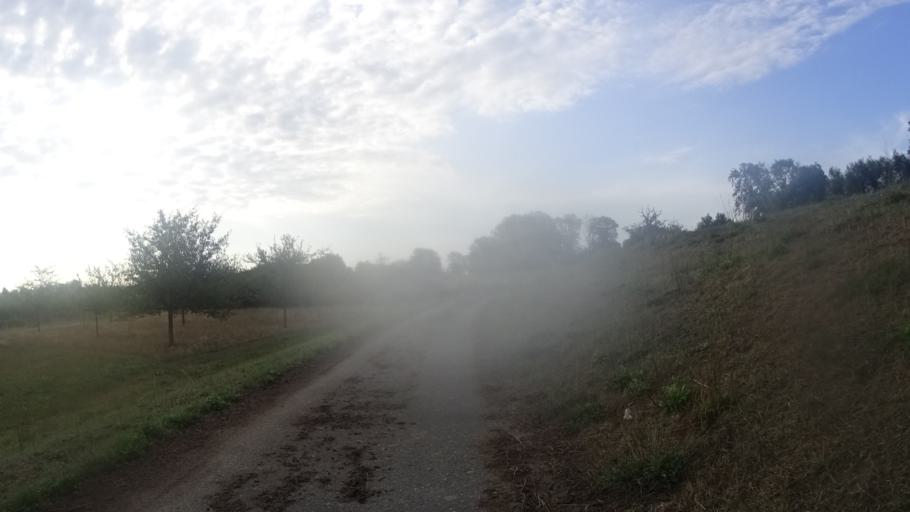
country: DE
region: Brandenburg
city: Lanz
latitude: 53.0408
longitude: 11.5807
